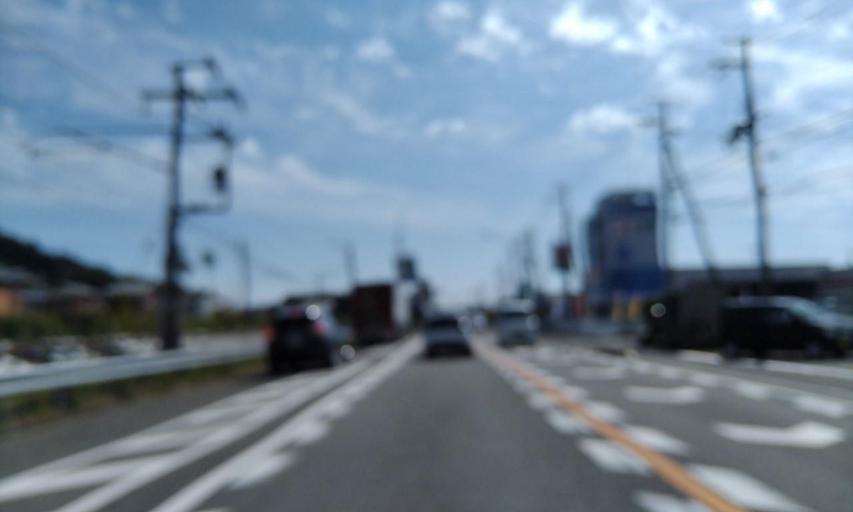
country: JP
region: Wakayama
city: Gobo
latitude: 33.9126
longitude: 135.1492
